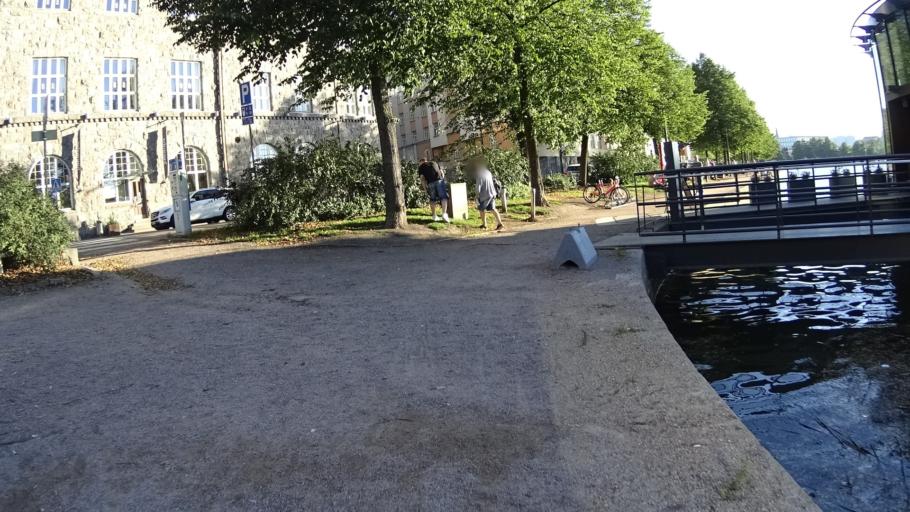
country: FI
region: Uusimaa
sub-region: Helsinki
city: Helsinki
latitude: 60.1794
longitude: 24.9473
